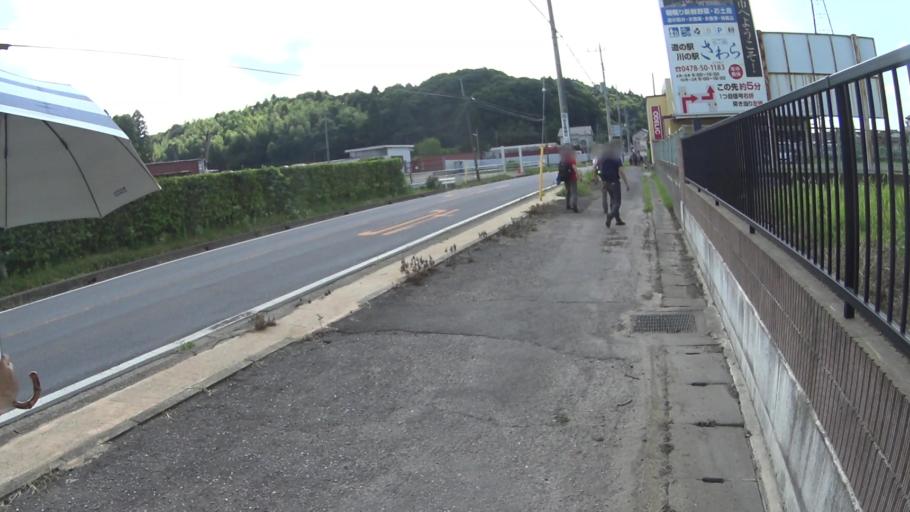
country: JP
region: Chiba
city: Sawara
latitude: 35.8838
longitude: 140.5209
